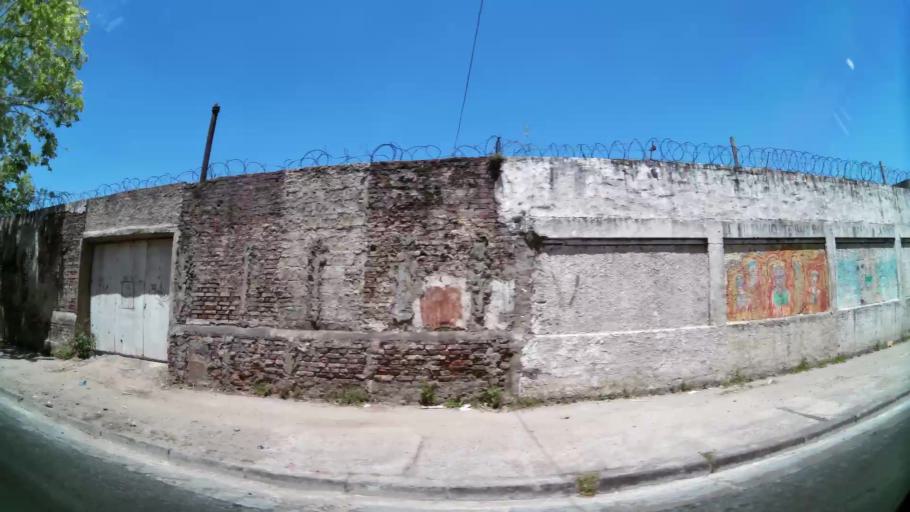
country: AR
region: Buenos Aires
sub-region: Partido de Avellaneda
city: Avellaneda
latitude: -34.6540
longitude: -58.3818
